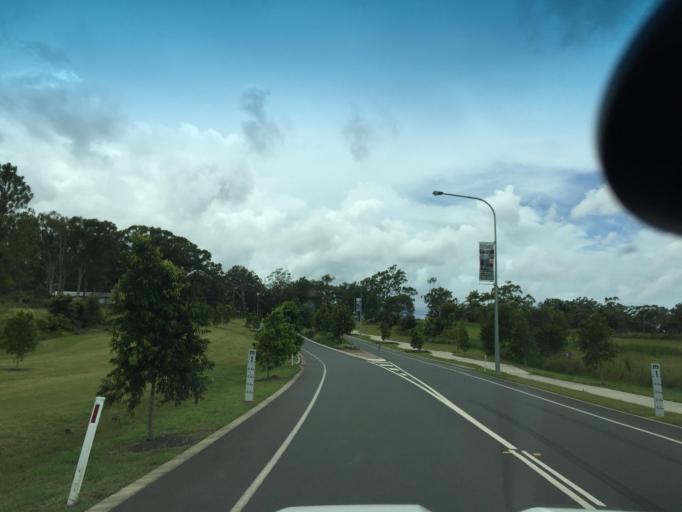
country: AU
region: Queensland
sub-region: Moreton Bay
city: Caboolture
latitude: -27.0589
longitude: 152.9390
